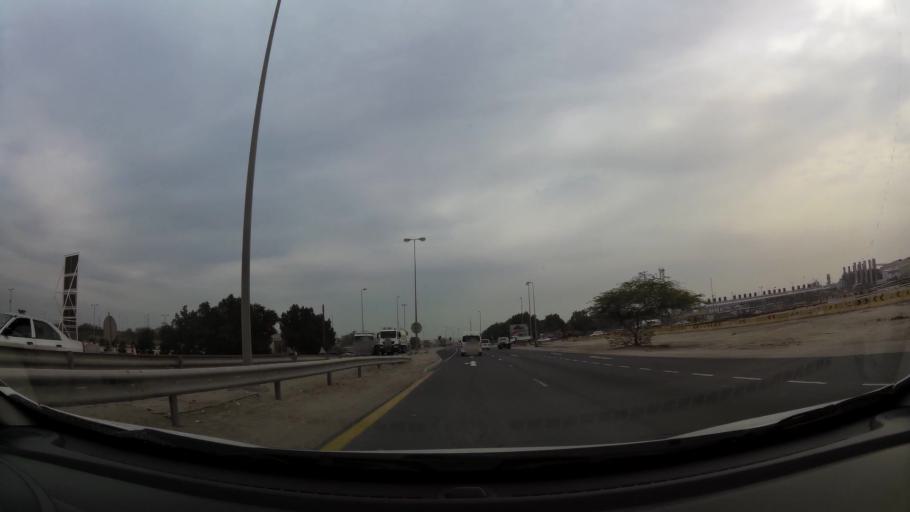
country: BH
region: Northern
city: Sitrah
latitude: 26.0992
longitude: 50.6051
